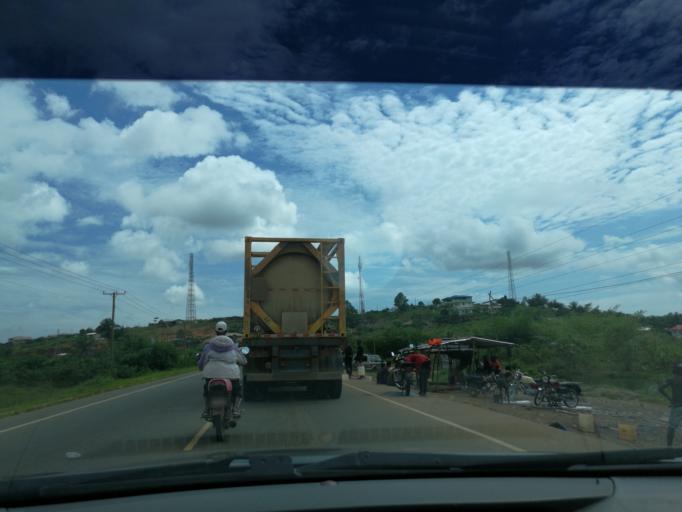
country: LR
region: Montserrado
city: Bensonville City
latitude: 6.3399
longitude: -10.6590
